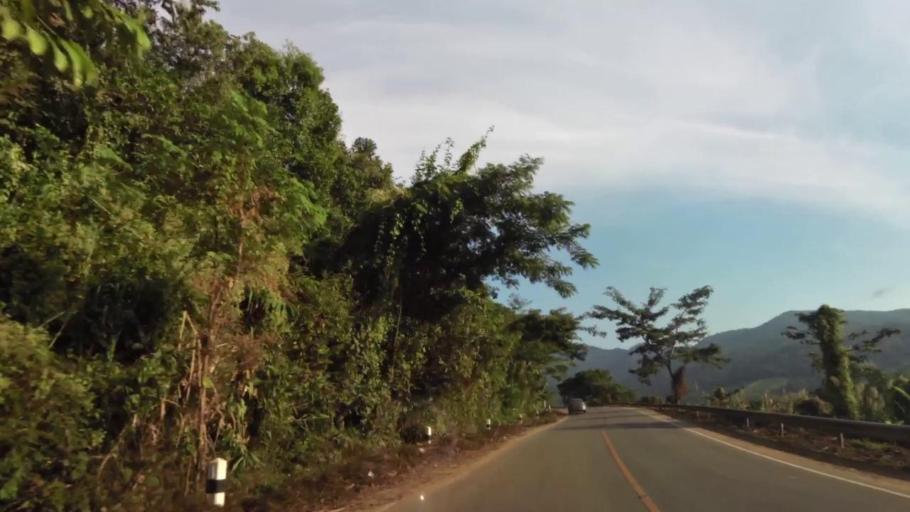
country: TH
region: Chiang Rai
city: Khun Tan
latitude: 19.8682
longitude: 100.4062
